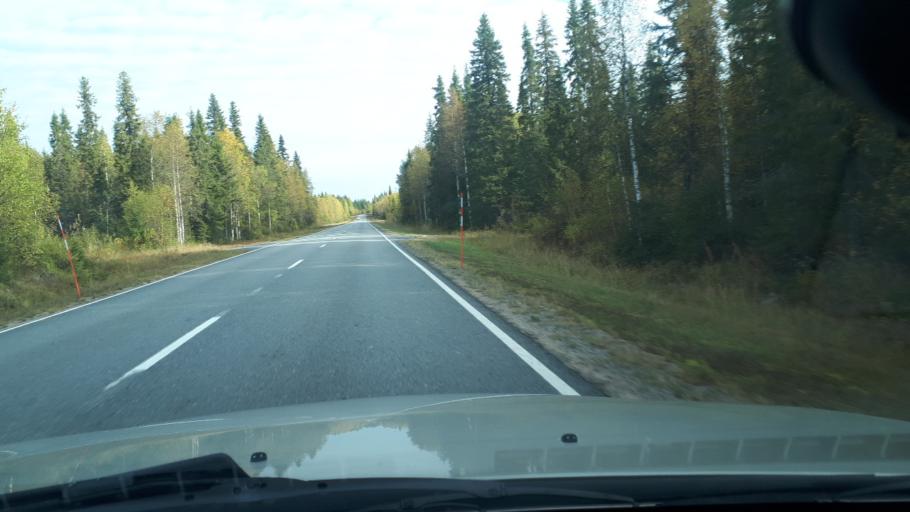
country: FI
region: Northern Ostrobothnia
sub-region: Oulu
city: Yli-Ii
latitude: 65.9456
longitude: 25.8993
